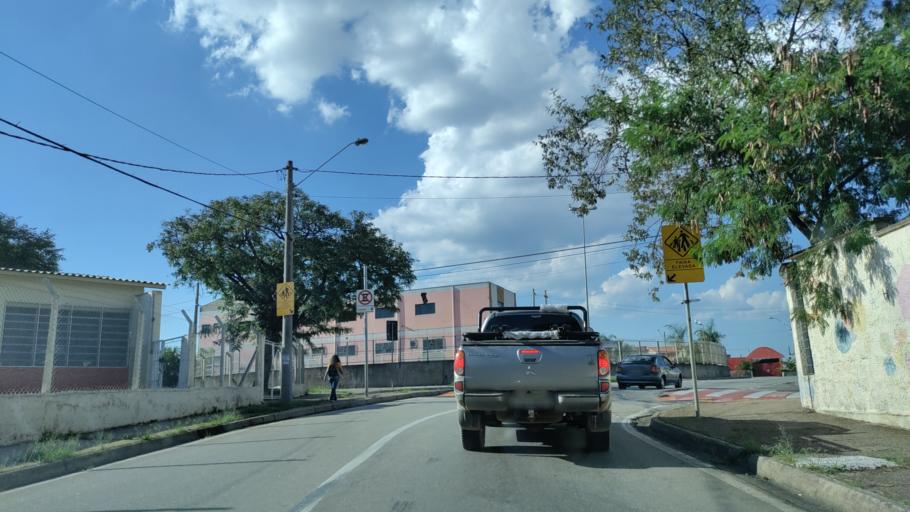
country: BR
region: Sao Paulo
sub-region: Sorocaba
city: Sorocaba
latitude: -23.4929
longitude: -47.4839
